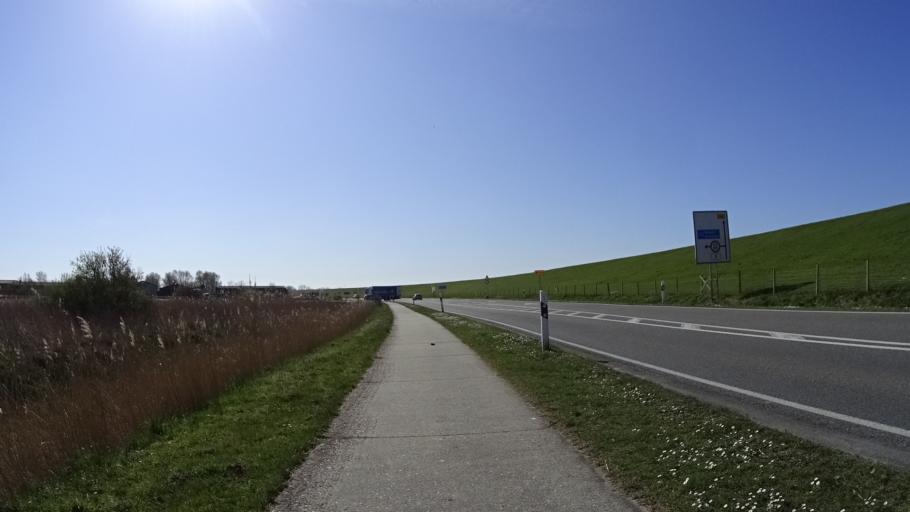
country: DE
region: Lower Saxony
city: Jemgum
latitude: 53.2378
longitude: 7.4076
